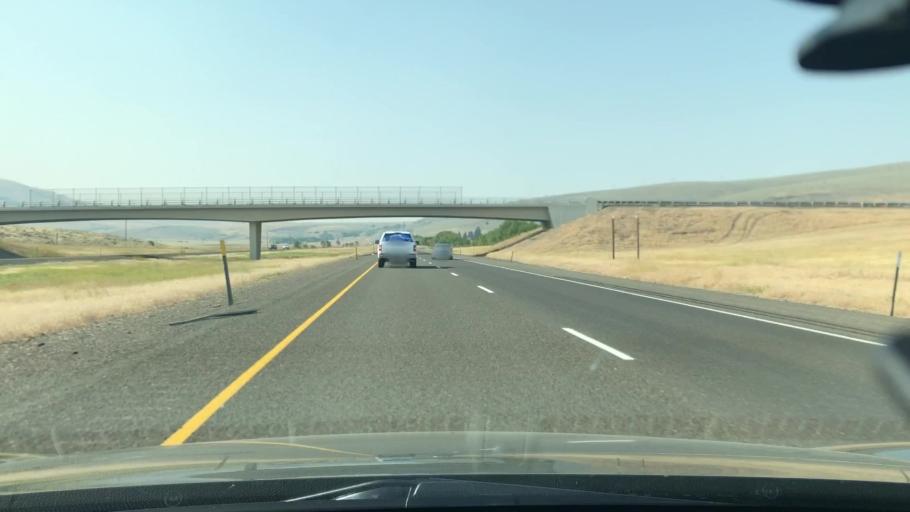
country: US
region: Oregon
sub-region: Union County
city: Union
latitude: 45.1230
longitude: -117.9621
